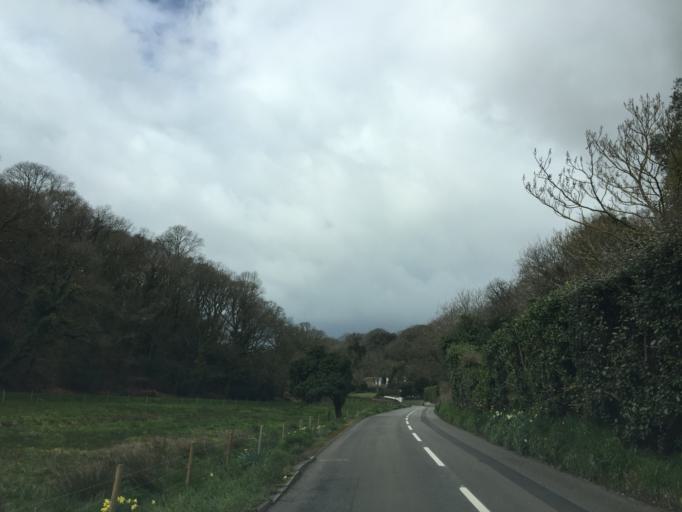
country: JE
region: St Helier
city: Saint Helier
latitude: 49.2114
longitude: -2.1621
